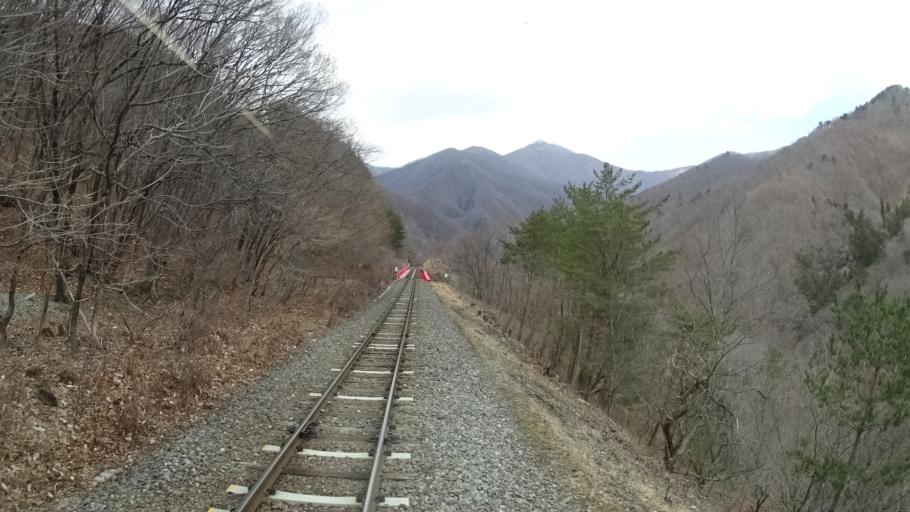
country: JP
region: Iwate
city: Kamaishi
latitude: 39.2748
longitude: 141.7206
